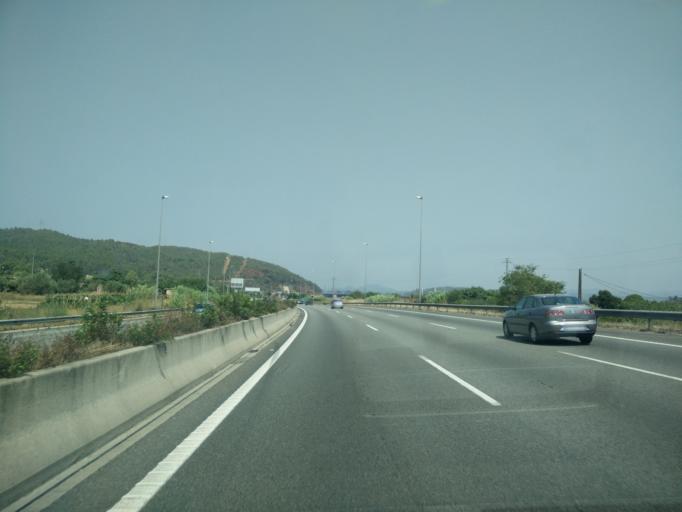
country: ES
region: Catalonia
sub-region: Provincia de Barcelona
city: Palleja
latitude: 41.4266
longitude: 2.0004
